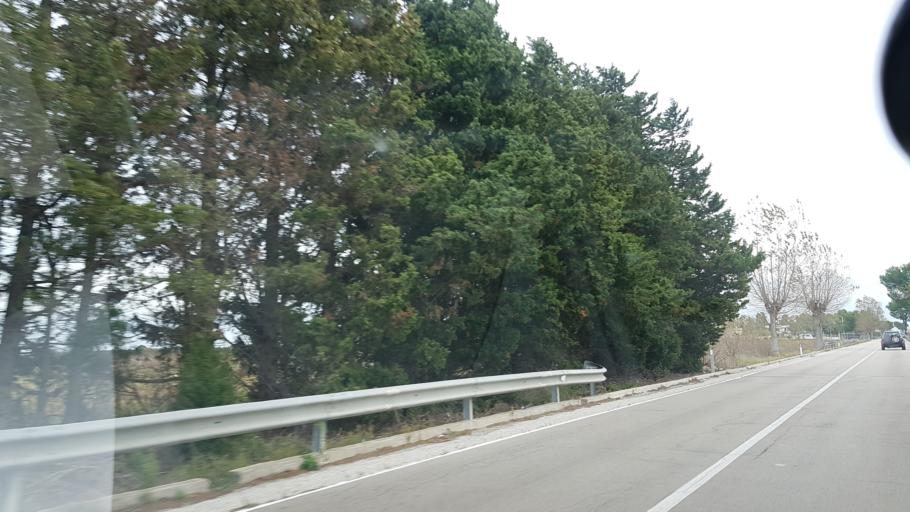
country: IT
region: Apulia
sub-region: Provincia di Brindisi
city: San Pancrazio Salentino
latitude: 40.4132
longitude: 17.8597
